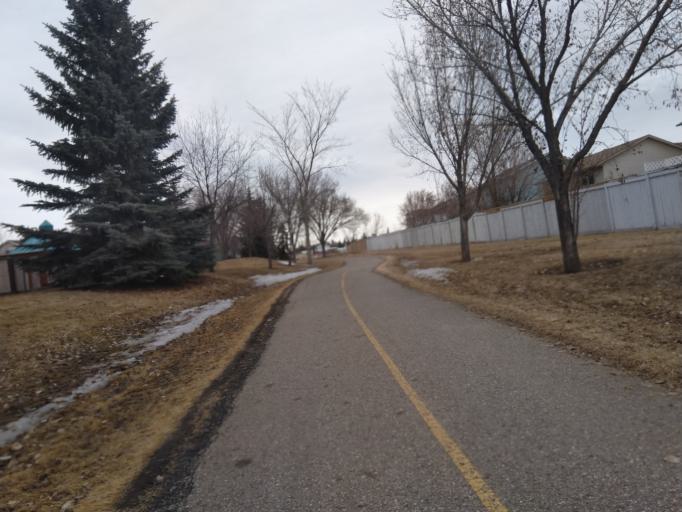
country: CA
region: Alberta
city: Calgary
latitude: 51.1559
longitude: -114.0481
